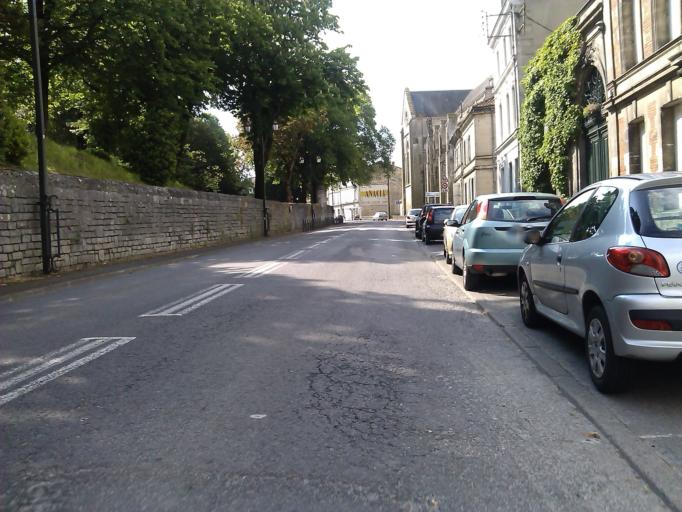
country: FR
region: Poitou-Charentes
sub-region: Departement de la Charente
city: Angouleme
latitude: 45.6514
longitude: 0.1455
